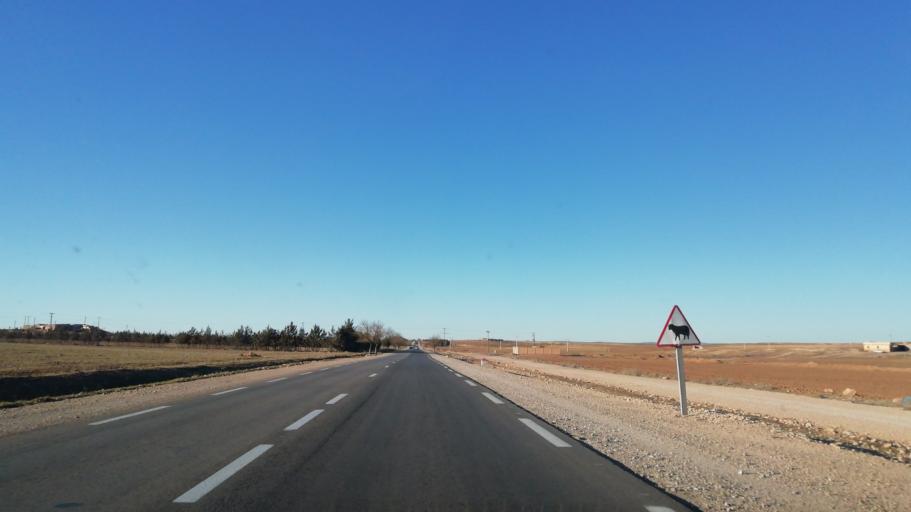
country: DZ
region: Tlemcen
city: Sebdou
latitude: 34.5168
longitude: -1.2867
